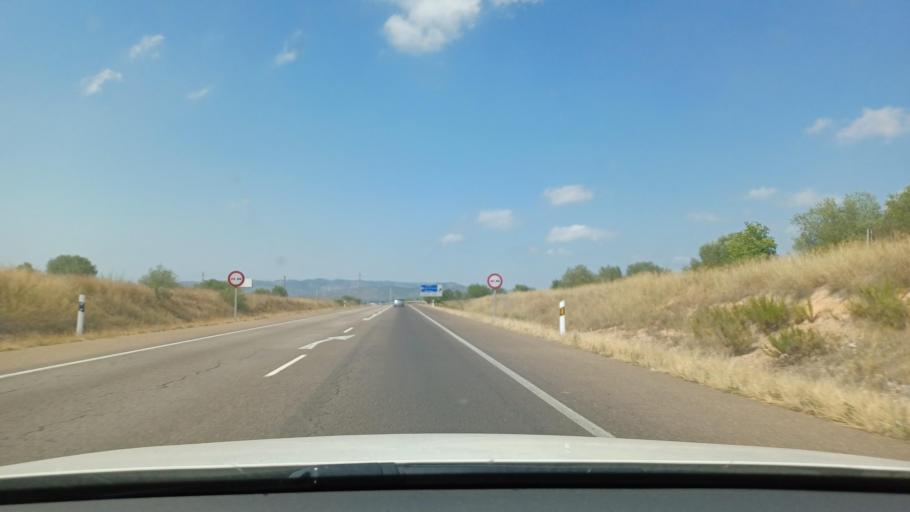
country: ES
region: Valencia
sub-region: Provincia de Castello
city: Vila-real
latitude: 39.9620
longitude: -0.0857
